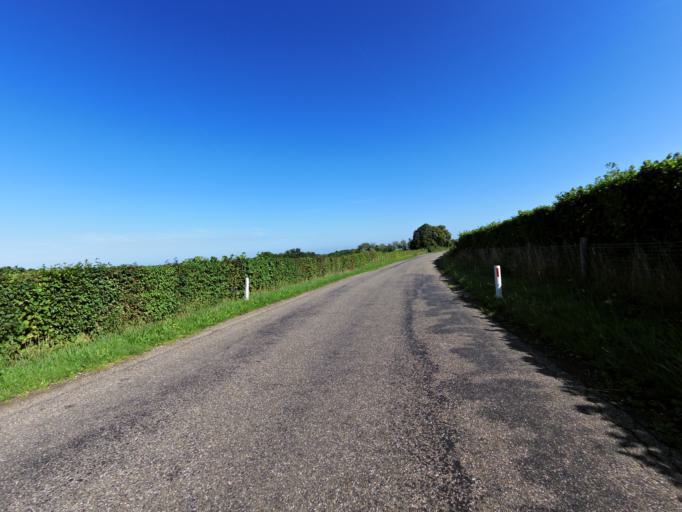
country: NL
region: Limburg
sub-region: Valkenburg aan de Geul
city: Schin op Geul
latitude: 50.7893
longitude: 5.8809
